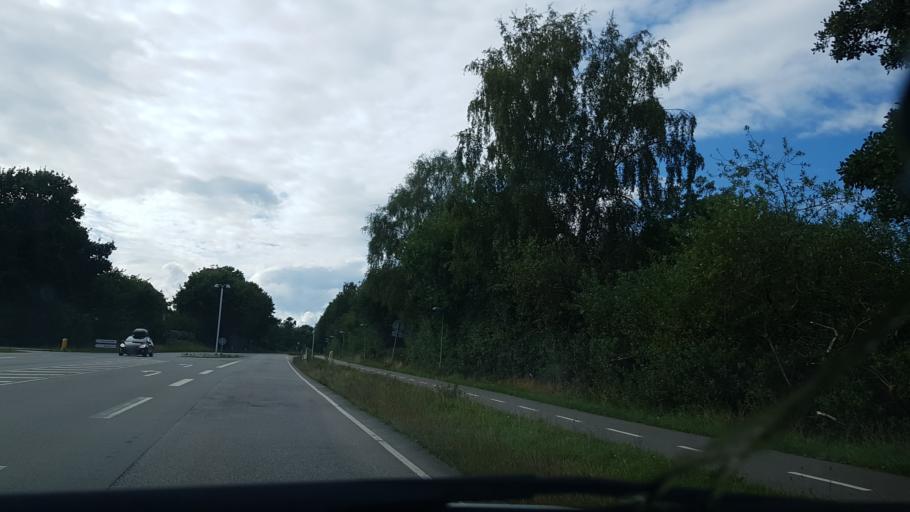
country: DK
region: Capital Region
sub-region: Fredensborg Kommune
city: Humlebaek
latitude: 55.9835
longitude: 12.5283
